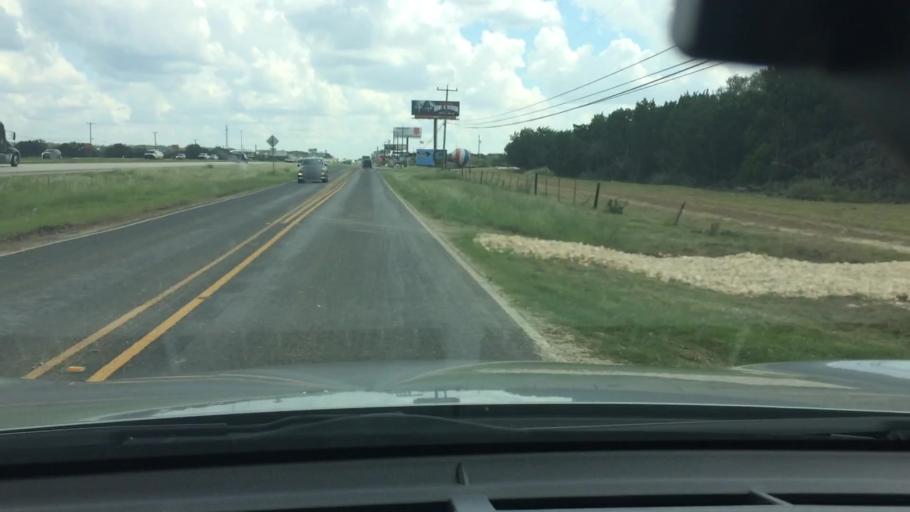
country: US
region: Texas
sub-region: Bexar County
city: Scenic Oaks
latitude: 29.7359
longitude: -98.6848
